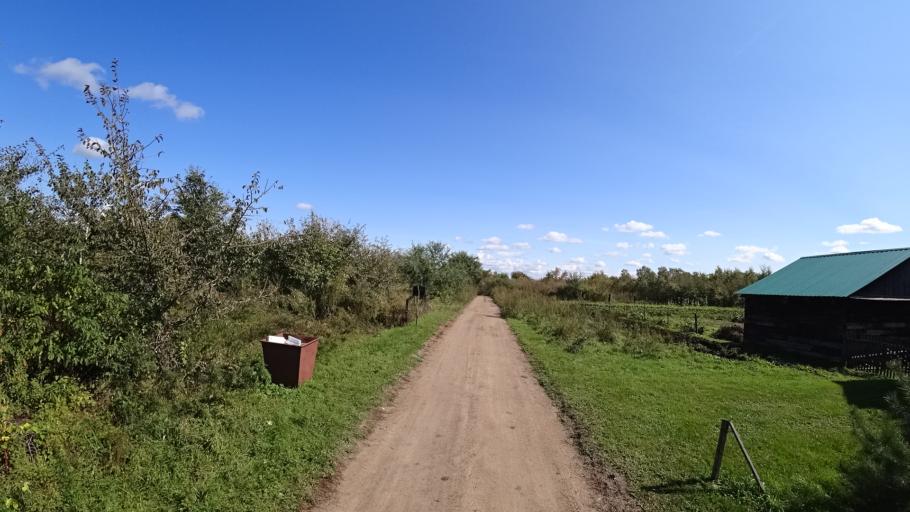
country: RU
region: Amur
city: Arkhara
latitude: 49.3993
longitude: 130.1264
